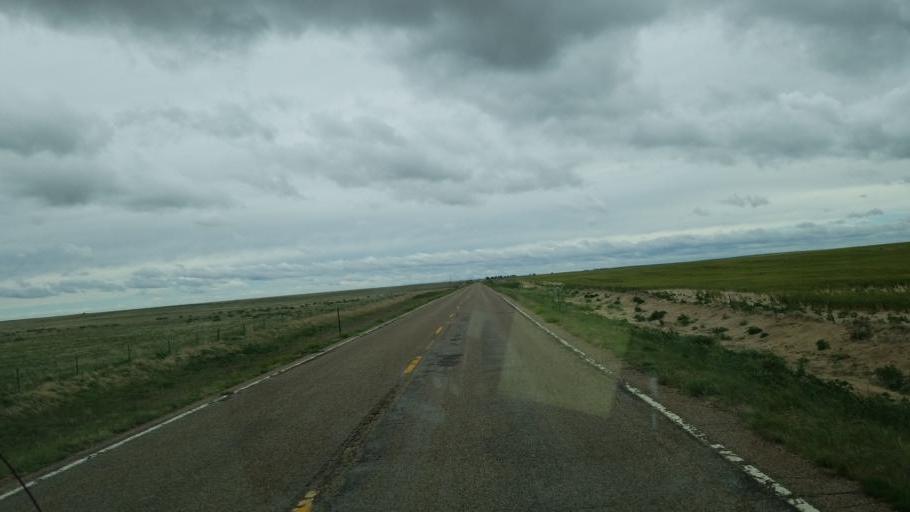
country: US
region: Colorado
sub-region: Lincoln County
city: Hugo
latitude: 38.8517
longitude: -103.6671
